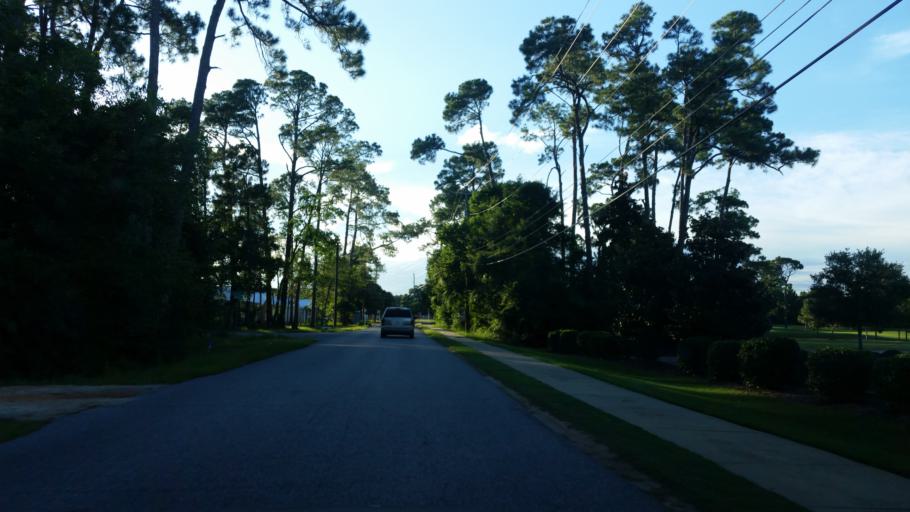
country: US
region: Florida
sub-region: Escambia County
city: Warrington
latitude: 30.3864
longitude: -87.2712
